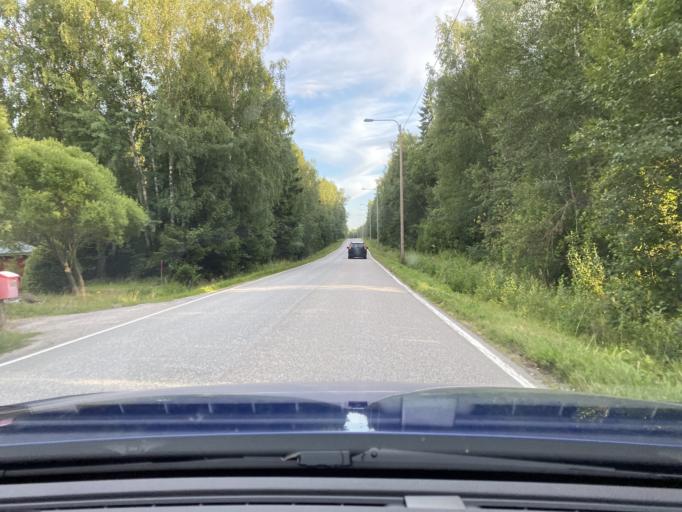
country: FI
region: Ostrobothnia
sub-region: Vaasa
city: Korsnaes
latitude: 62.9513
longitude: 21.1762
